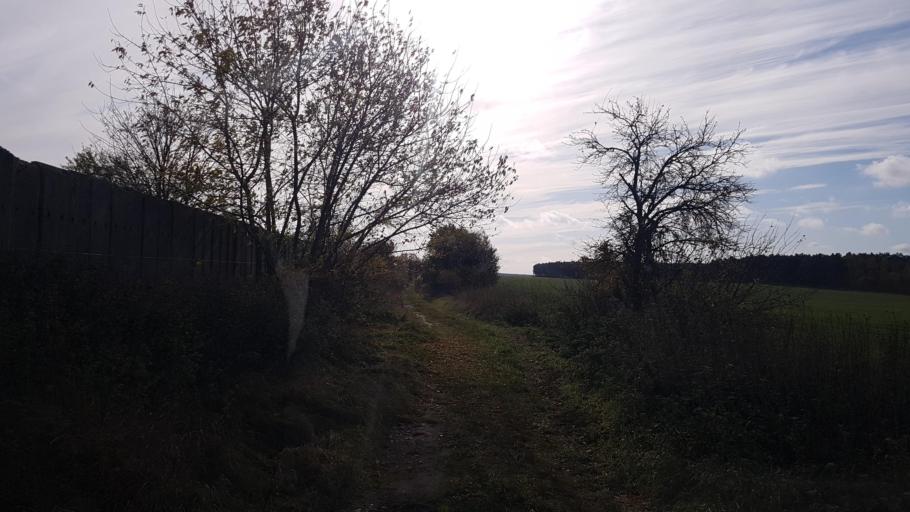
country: DE
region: Saxony-Anhalt
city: Zahna
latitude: 51.9750
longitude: 12.8276
